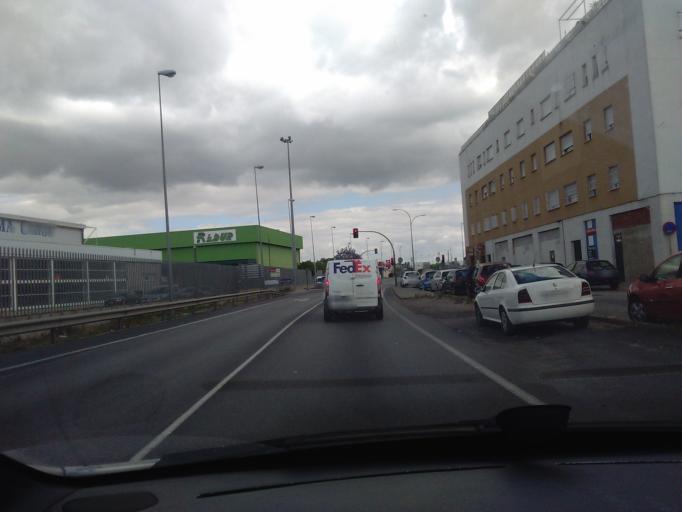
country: ES
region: Andalusia
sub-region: Provincia de Sevilla
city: Sevilla
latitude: 37.3819
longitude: -5.9398
